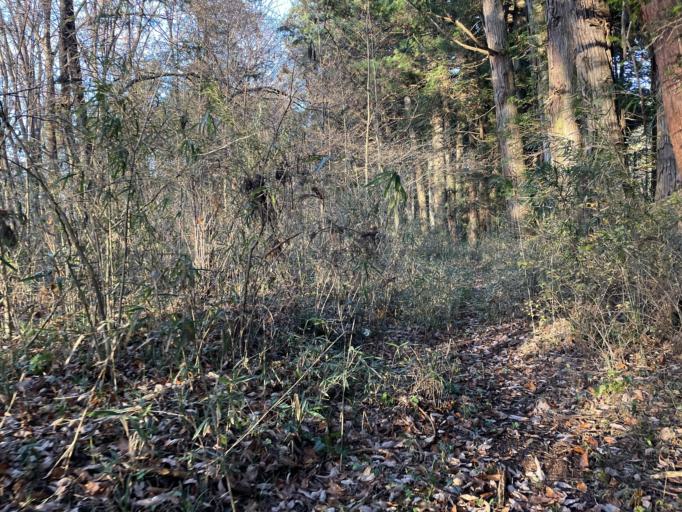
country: JP
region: Tochigi
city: Imaichi
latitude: 36.6649
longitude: 139.7209
